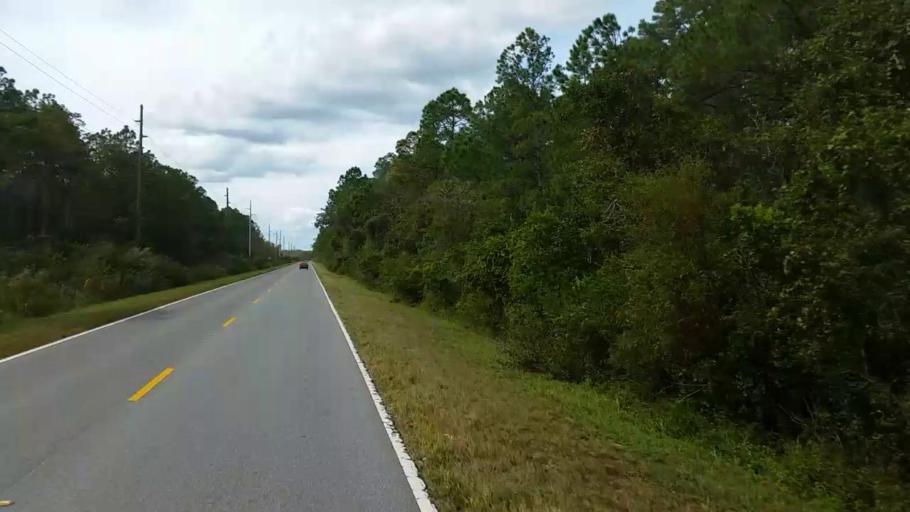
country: US
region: Florida
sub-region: Lake County
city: Four Corners
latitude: 28.3700
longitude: -81.7108
